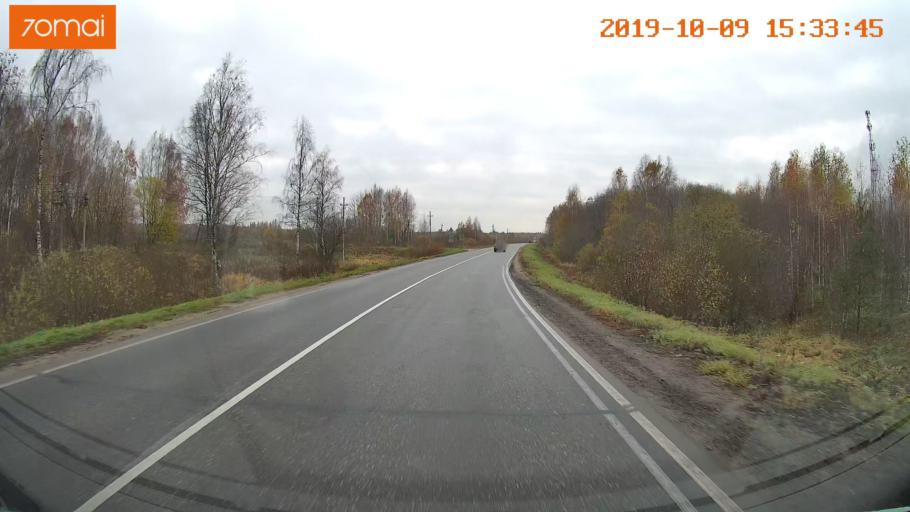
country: RU
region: Kostroma
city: Oktyabr'skiy
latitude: 57.9476
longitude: 41.2578
